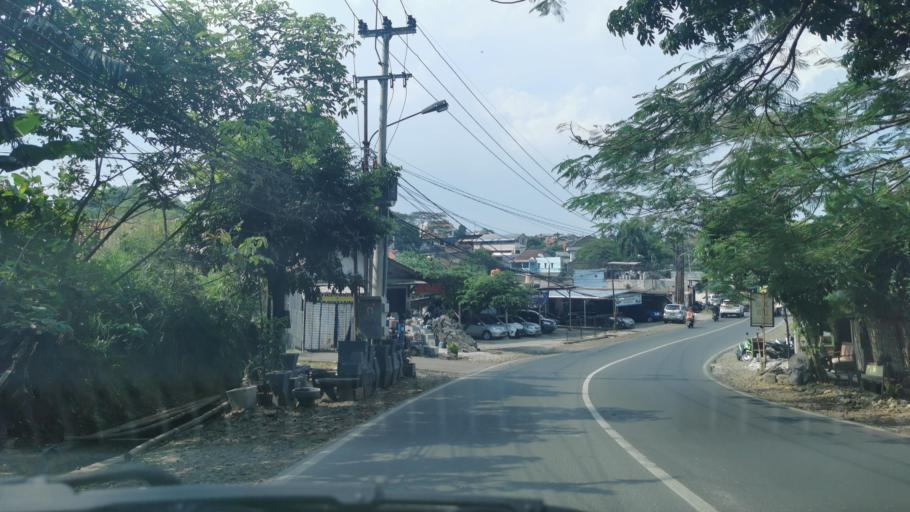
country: ID
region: West Java
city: Depok
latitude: -6.4073
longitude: 106.8353
